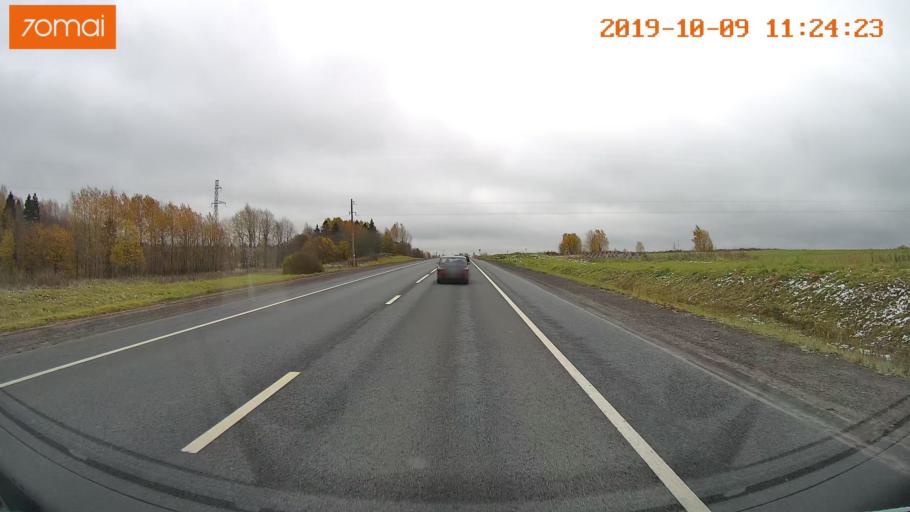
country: RU
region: Vologda
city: Vologda
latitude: 59.1119
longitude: 39.9794
